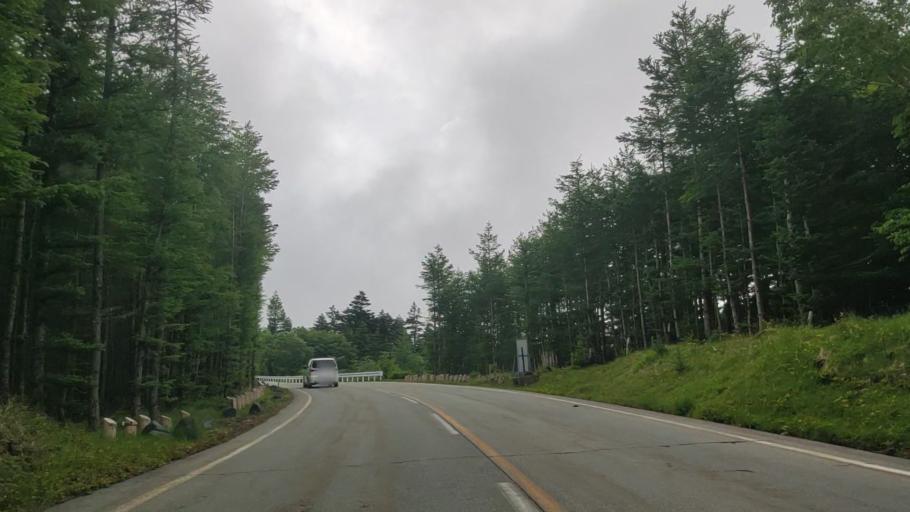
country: JP
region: Yamanashi
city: Fujikawaguchiko
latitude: 35.3882
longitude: 138.6906
